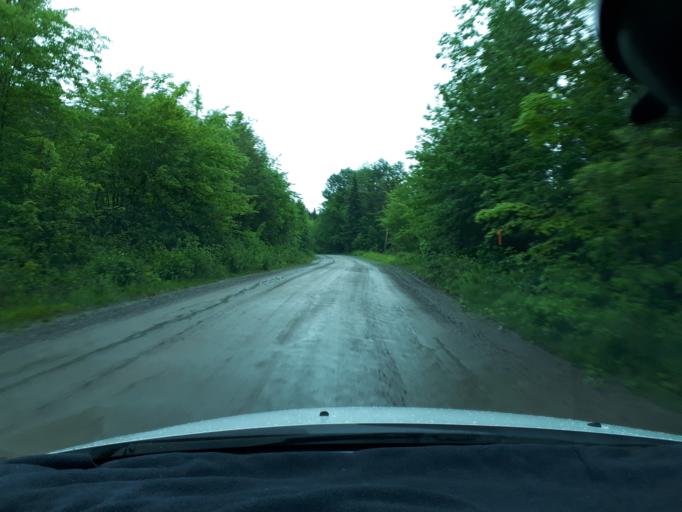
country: CA
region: Nova Scotia
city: Sydney Mines
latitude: 46.2668
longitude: -60.4746
